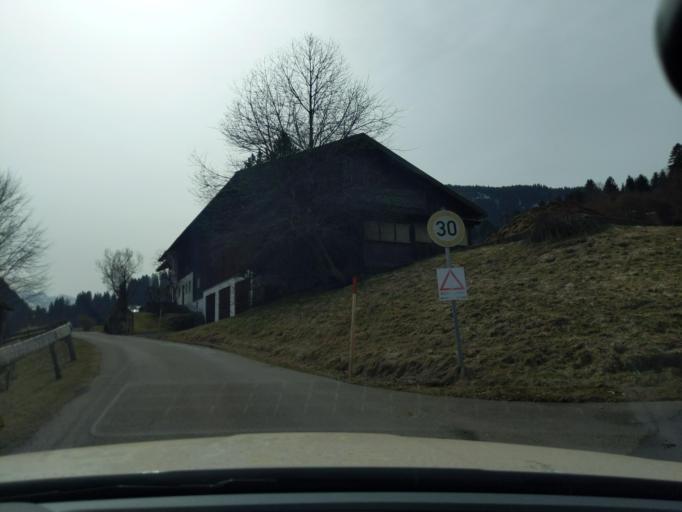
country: DE
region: Bavaria
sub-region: Swabia
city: Obermaiselstein
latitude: 47.4463
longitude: 10.2352
